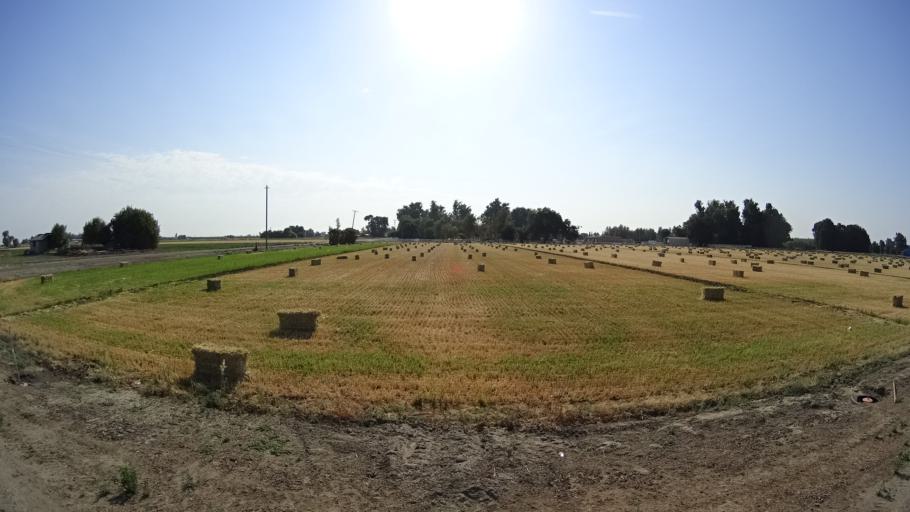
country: US
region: California
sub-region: Fresno County
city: Riverdale
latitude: 36.3727
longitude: -119.8252
